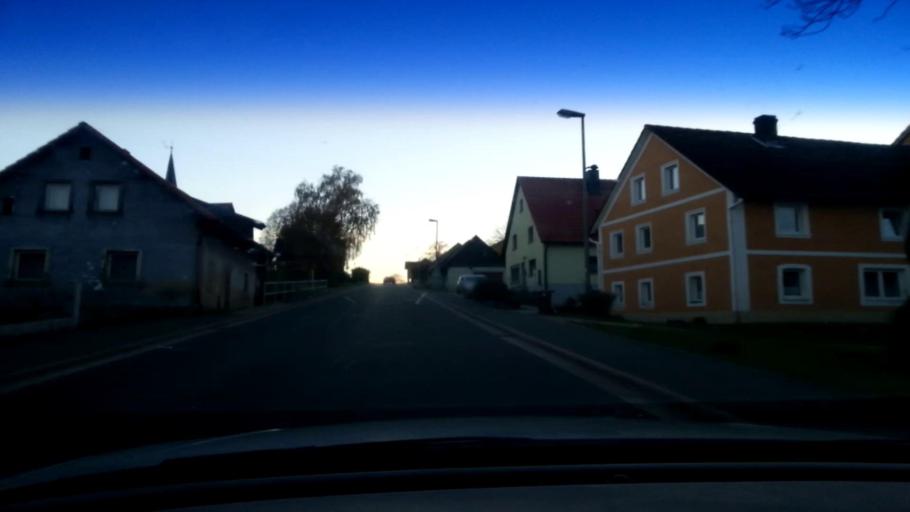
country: DE
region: Bavaria
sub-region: Upper Franconia
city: Poxdorf
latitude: 49.8726
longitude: 11.0924
